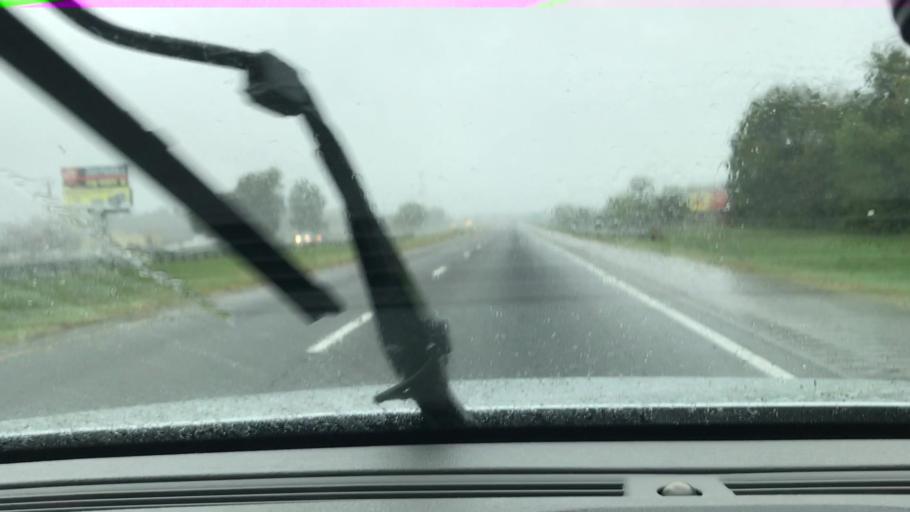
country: US
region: Alabama
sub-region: Limestone County
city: Ardmore
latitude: 34.9640
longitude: -86.8872
